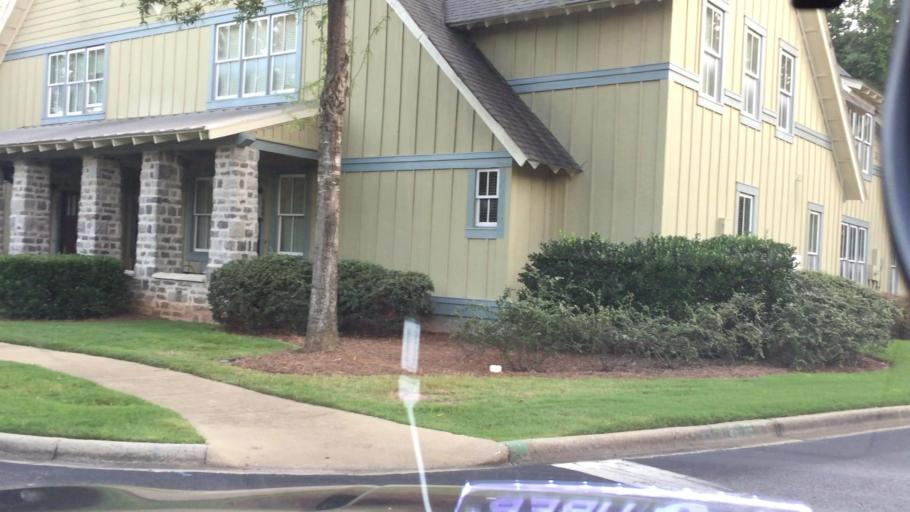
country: US
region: Alabama
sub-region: Lee County
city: Auburn
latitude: 32.6194
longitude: -85.4701
